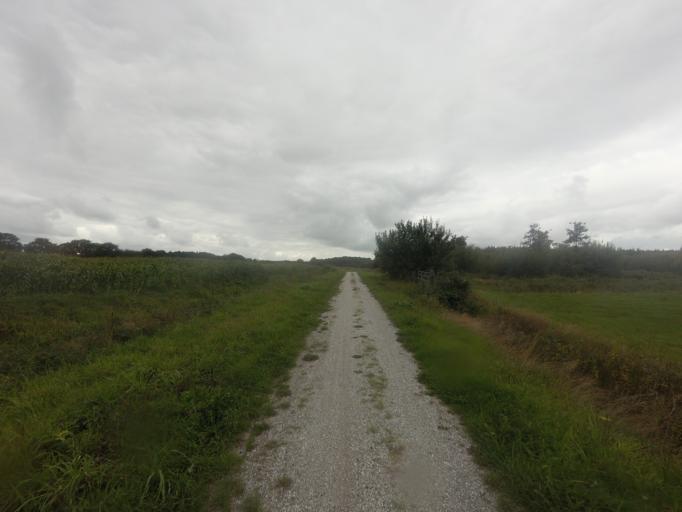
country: NL
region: Friesland
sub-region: Gemeente Weststellingwerf
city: Noordwolde
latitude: 52.9362
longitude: 6.1746
